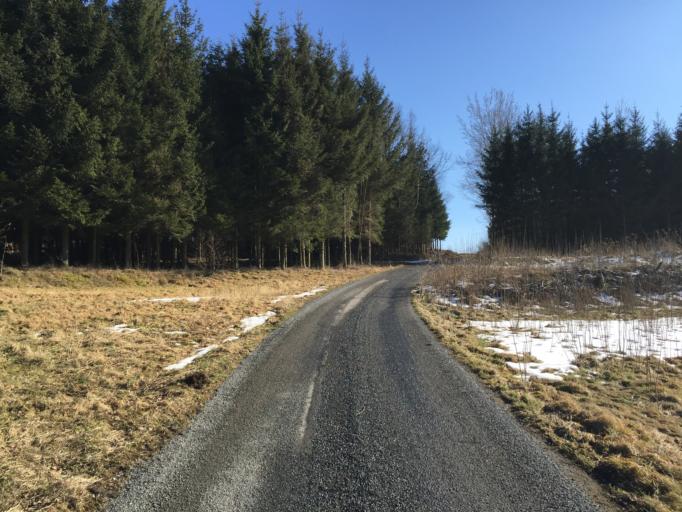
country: AT
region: Lower Austria
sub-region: Politischer Bezirk Gmund
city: Weitra
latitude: 48.6702
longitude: 14.9299
